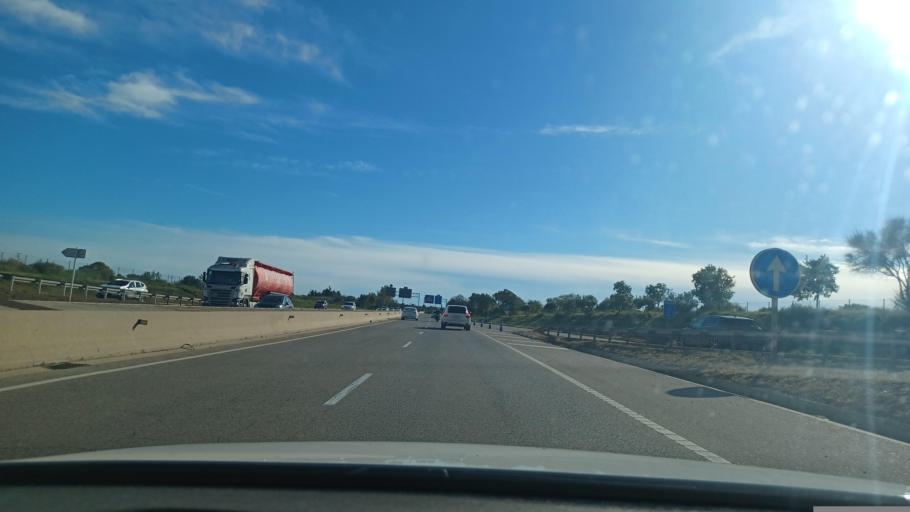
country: ES
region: Catalonia
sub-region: Provincia de Tarragona
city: Vila-seca
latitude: 41.1445
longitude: 1.1411
